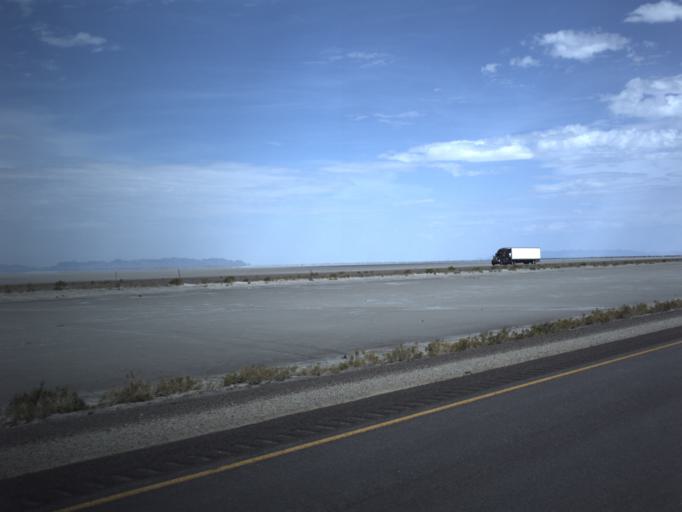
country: US
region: Utah
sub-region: Tooele County
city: Wendover
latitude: 40.7363
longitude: -113.7461
